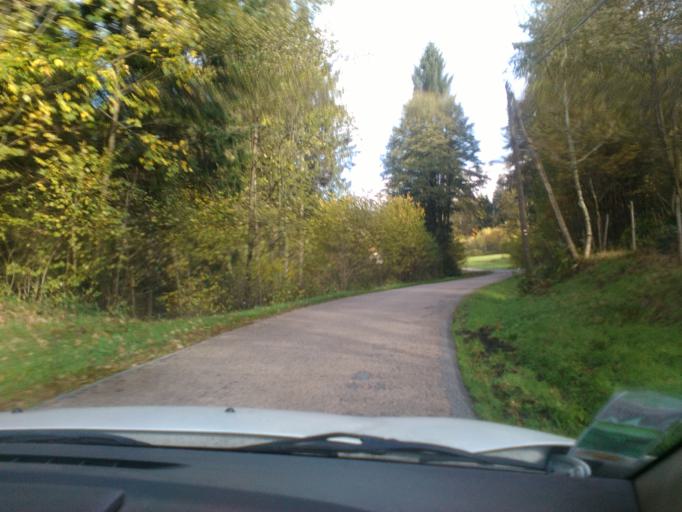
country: FR
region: Lorraine
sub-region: Departement des Vosges
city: Saulxures-sur-Moselotte
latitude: 47.9631
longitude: 6.7866
